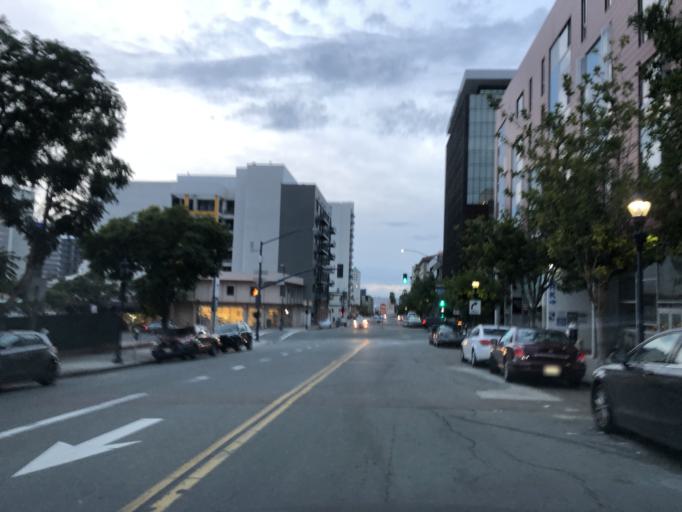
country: US
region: California
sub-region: San Diego County
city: San Diego
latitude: 32.7221
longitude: -117.1594
